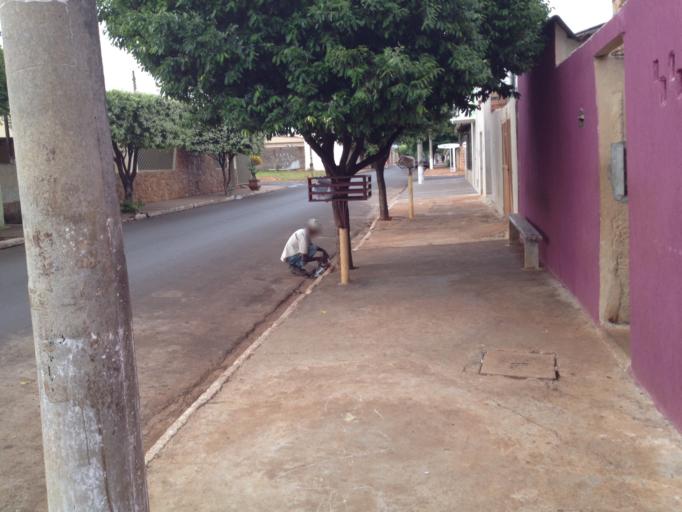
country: BR
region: Sao Paulo
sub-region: Barrinha
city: Barrinha
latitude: -21.1954
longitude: -48.1622
